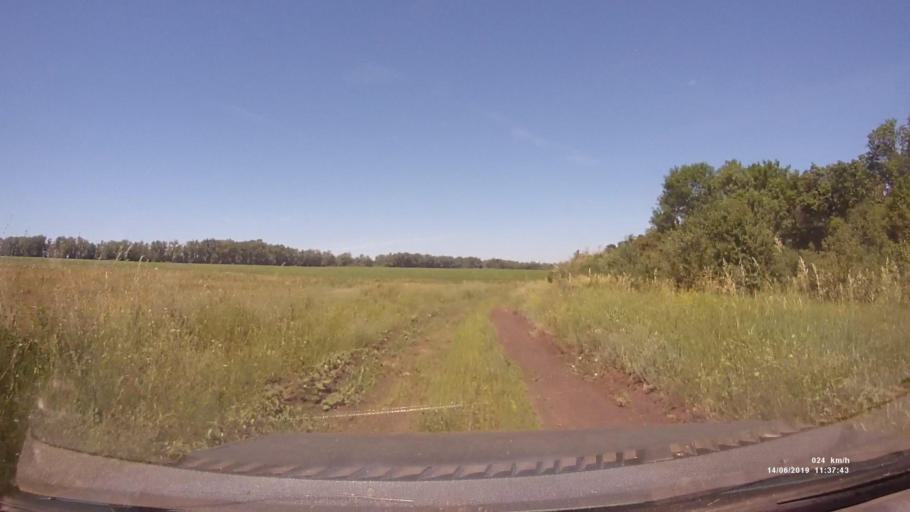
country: RU
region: Rostov
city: Kazanskaya
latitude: 49.8638
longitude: 41.3714
